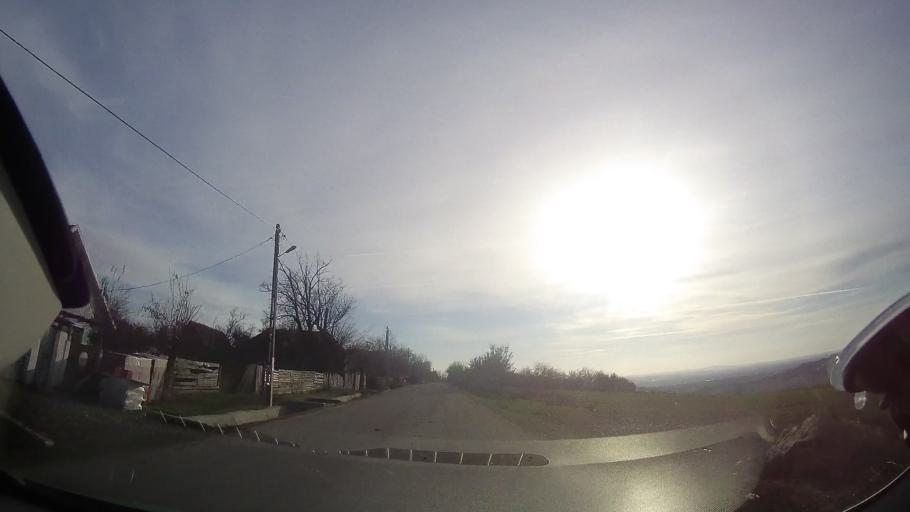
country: RO
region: Bihor
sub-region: Comuna Sarbi
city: Burzuc
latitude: 47.1202
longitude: 22.1795
